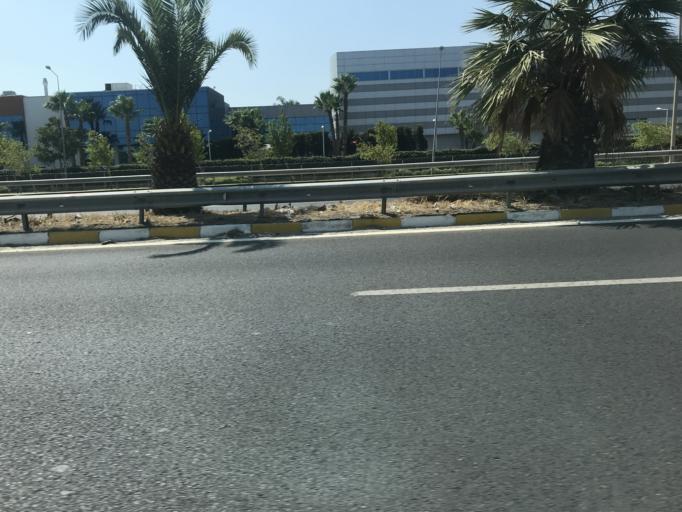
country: TR
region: Izmir
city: Karsiyaka
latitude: 38.3961
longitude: 27.0524
